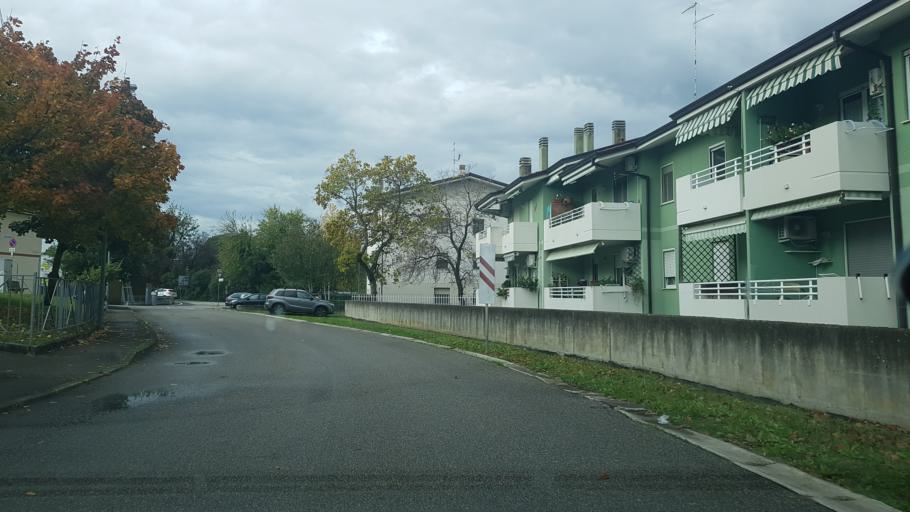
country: IT
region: Friuli Venezia Giulia
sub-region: Provincia di Gorizia
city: Ronchi dei Legionari
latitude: 45.8228
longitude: 13.5152
